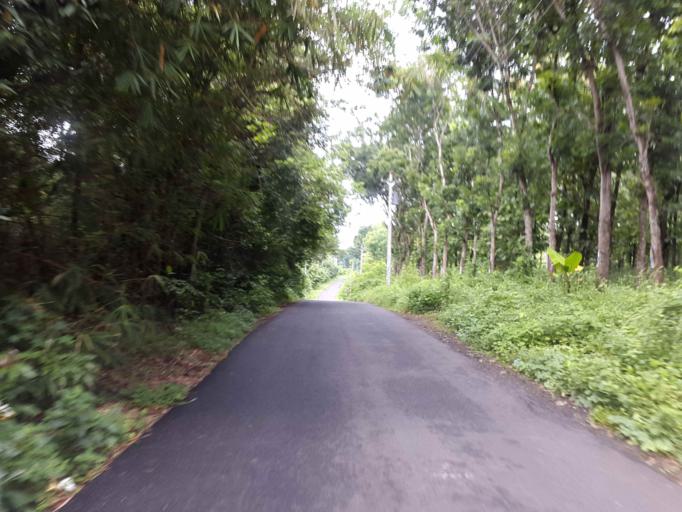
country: ID
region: Central Java
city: Randudongkal
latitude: -7.0445
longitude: 109.3629
